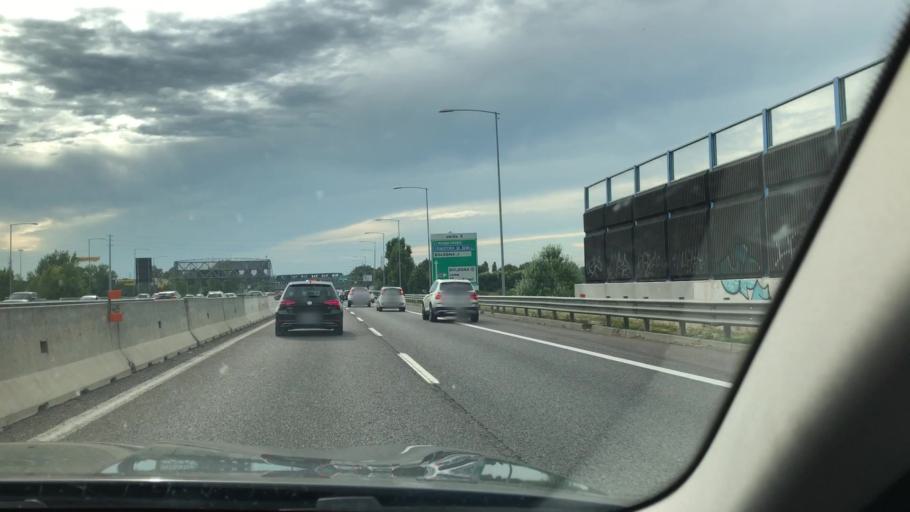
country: IT
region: Emilia-Romagna
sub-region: Provincia di Bologna
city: Trebbo
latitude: 44.5302
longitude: 11.3437
